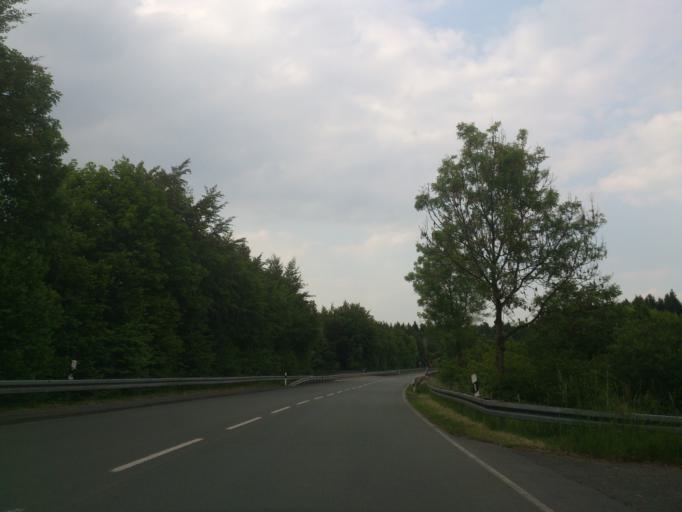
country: DE
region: North Rhine-Westphalia
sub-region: Regierungsbezirk Detmold
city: Bad Driburg
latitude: 51.6776
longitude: 8.9642
